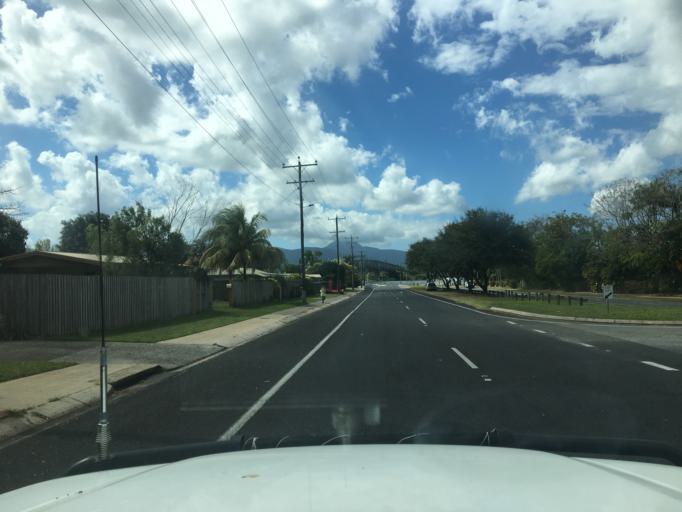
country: AU
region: Queensland
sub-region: Cairns
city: Woree
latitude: -16.9675
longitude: 145.7439
